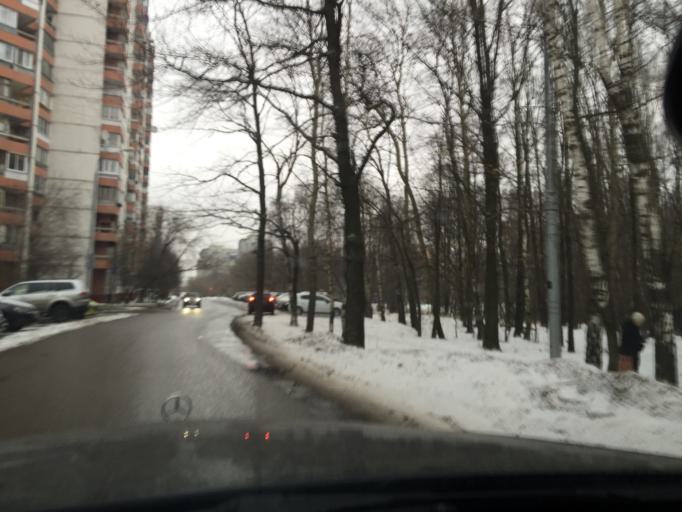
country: RU
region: Moscow
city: Troparevo
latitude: 55.6410
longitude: 37.4781
